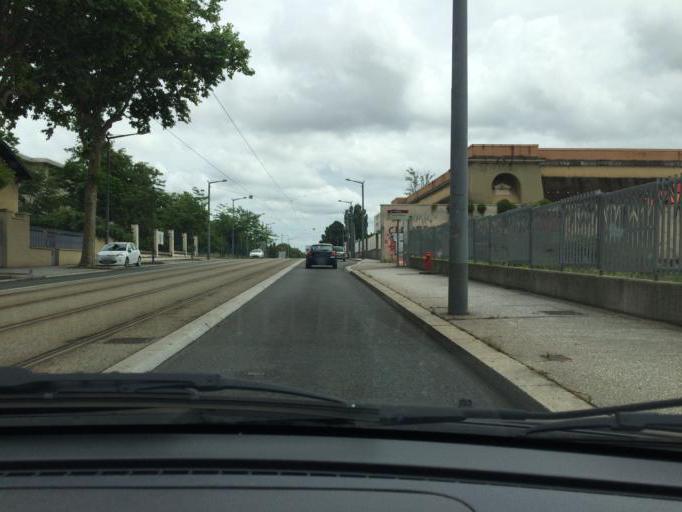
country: FR
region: Rhone-Alpes
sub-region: Departement du Rhone
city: Bron
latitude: 45.7395
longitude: 4.8905
